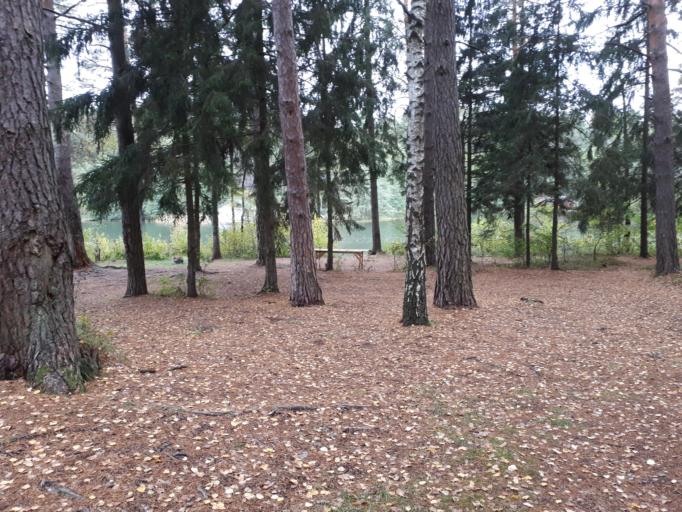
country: LT
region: Alytaus apskritis
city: Druskininkai
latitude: 54.0928
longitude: 23.9156
